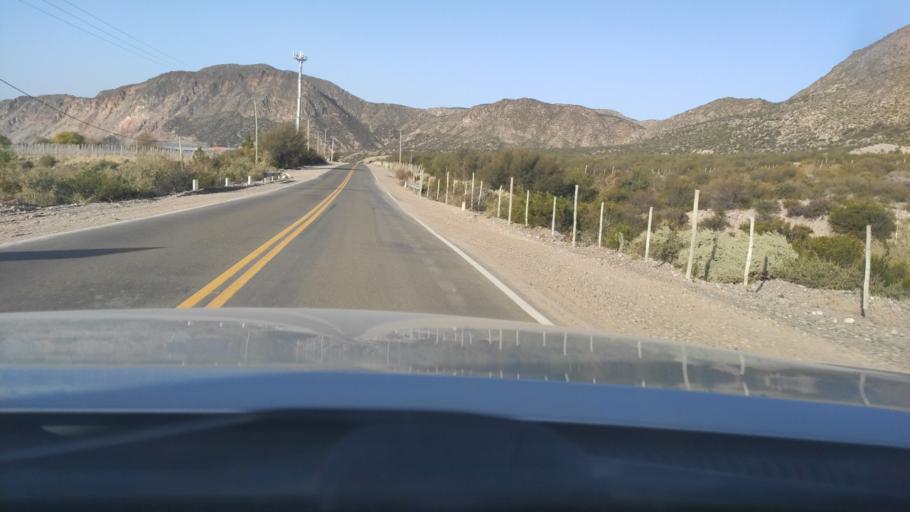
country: AR
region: San Juan
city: Villa Media Agua
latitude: -32.0031
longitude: -68.7642
